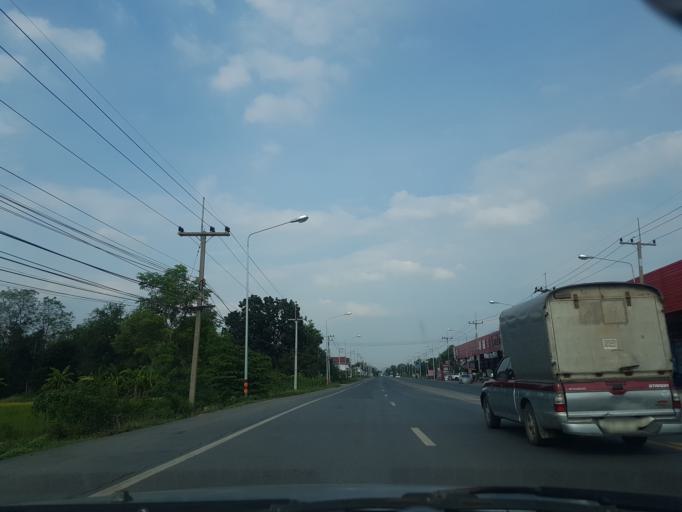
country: TH
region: Sara Buri
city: Ban Mo
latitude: 14.6011
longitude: 100.7350
